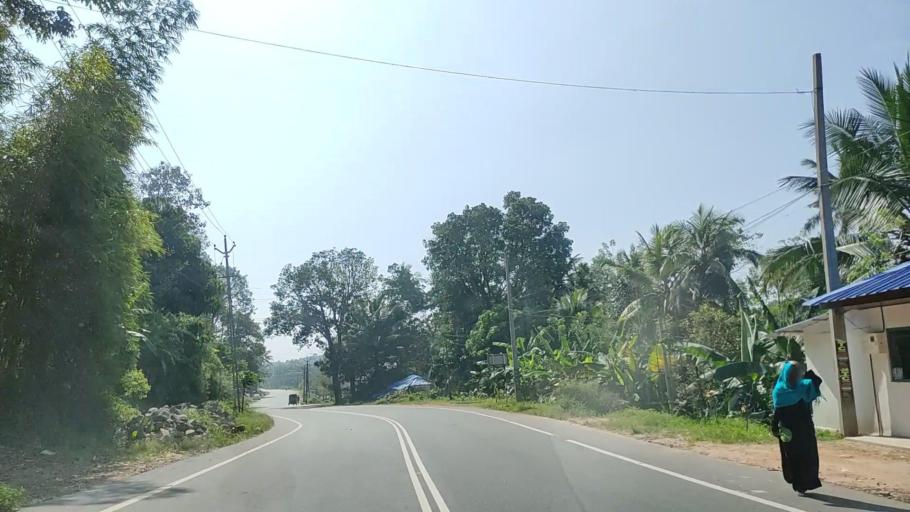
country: IN
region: Kerala
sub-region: Kollam
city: Punalur
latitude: 8.9147
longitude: 77.0454
